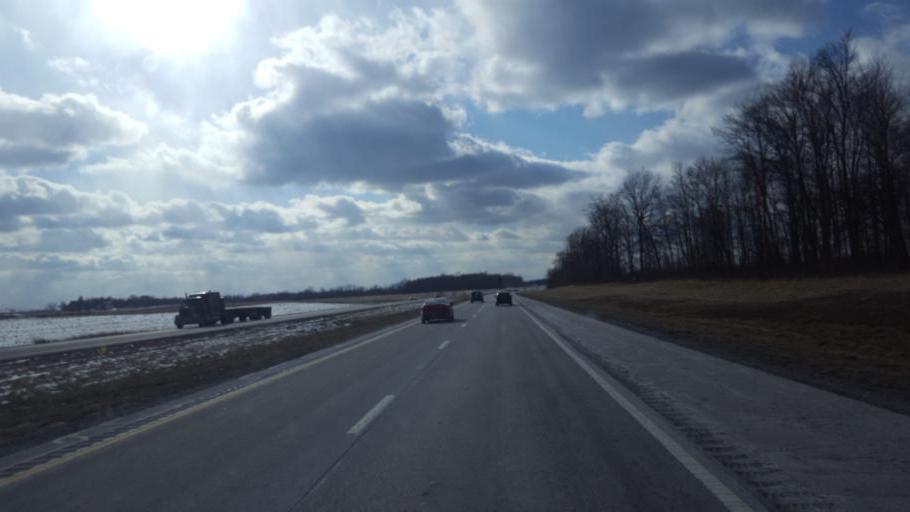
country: US
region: Ohio
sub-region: Crawford County
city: Crestline
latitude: 40.7620
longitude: -82.7111
